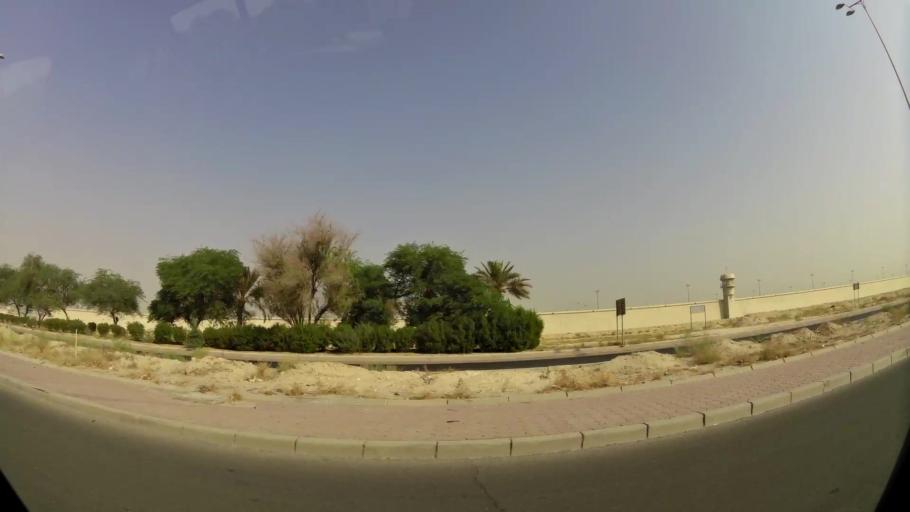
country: KW
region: Al Asimah
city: Ar Rabiyah
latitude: 29.2747
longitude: 47.8563
